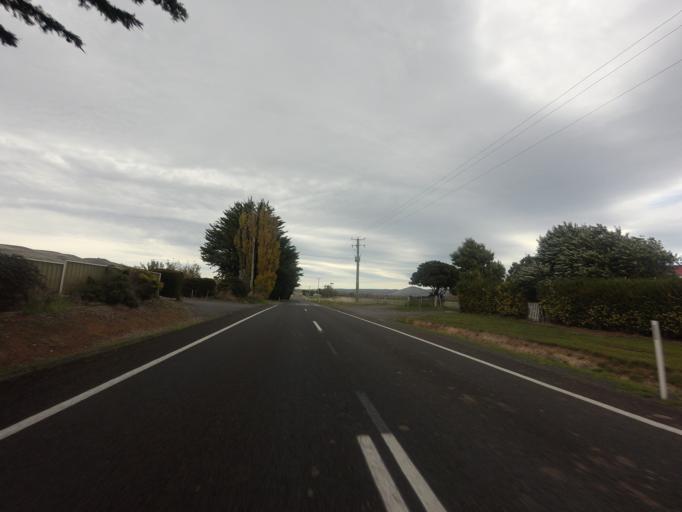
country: AU
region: Tasmania
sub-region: Derwent Valley
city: New Norfolk
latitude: -42.4984
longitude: 146.7315
